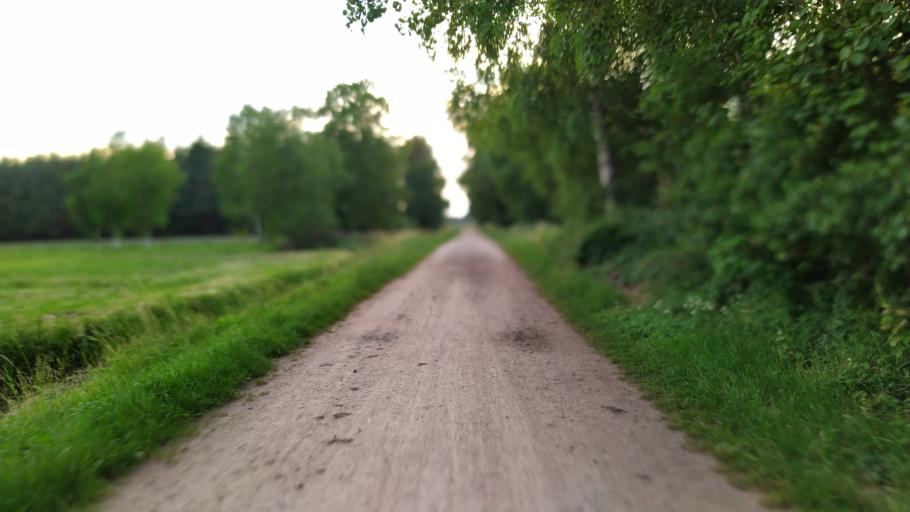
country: DE
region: Lower Saxony
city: Buxtehude
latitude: 53.4815
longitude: 9.6578
